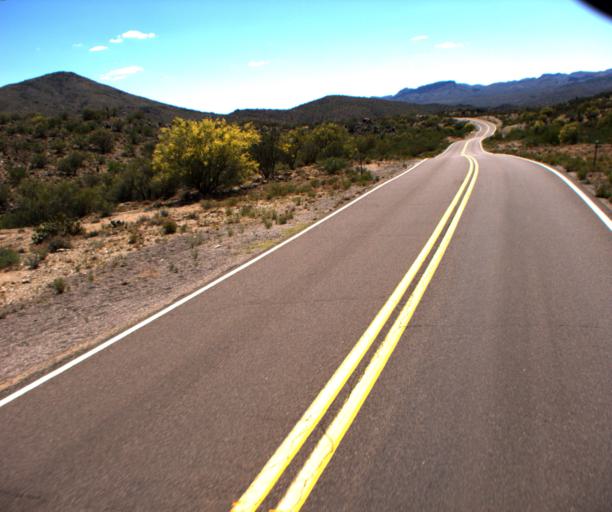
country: US
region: Arizona
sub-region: Yavapai County
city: Bagdad
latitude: 34.4783
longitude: -113.2059
